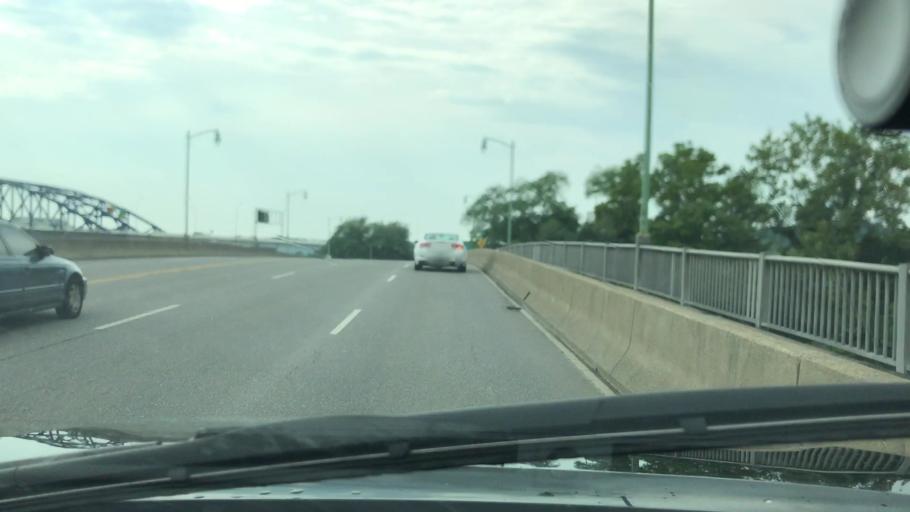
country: US
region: West Virginia
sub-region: Kanawha County
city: Charleston
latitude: 38.3545
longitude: -81.6438
